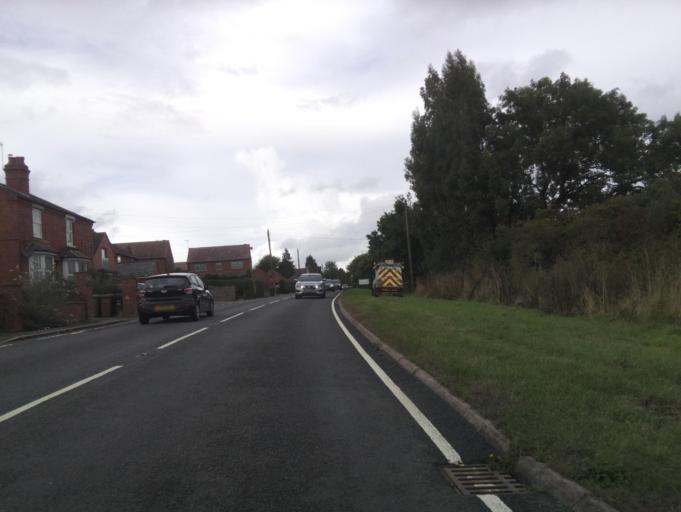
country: GB
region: England
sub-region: Worcestershire
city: Droitwich
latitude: 52.3105
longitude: -2.1782
